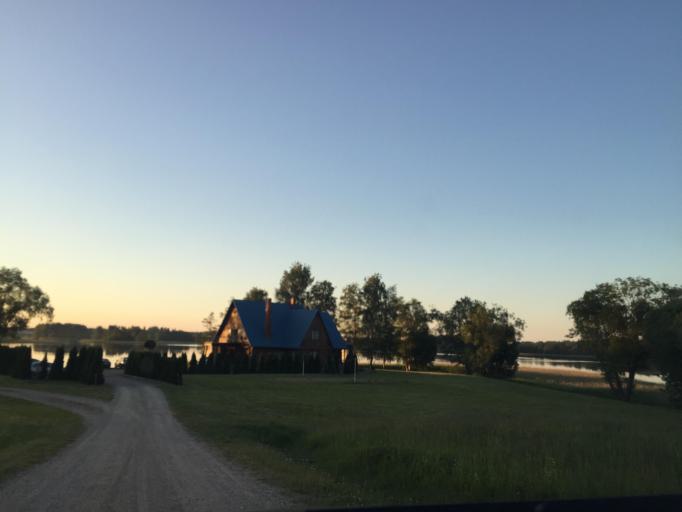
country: LV
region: Rezekne
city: Rezekne
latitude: 56.3634
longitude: 27.4158
